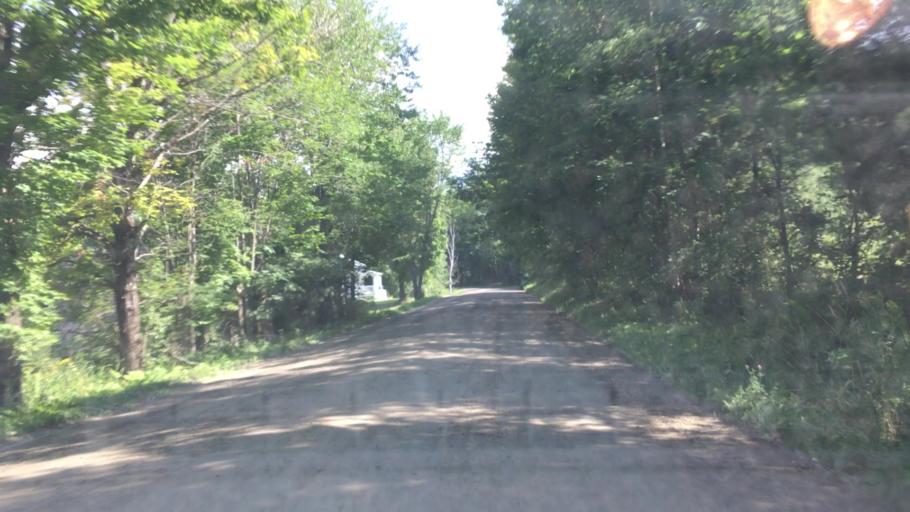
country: US
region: New Hampshire
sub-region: Grafton County
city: Woodsville
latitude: 44.1353
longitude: -71.9693
